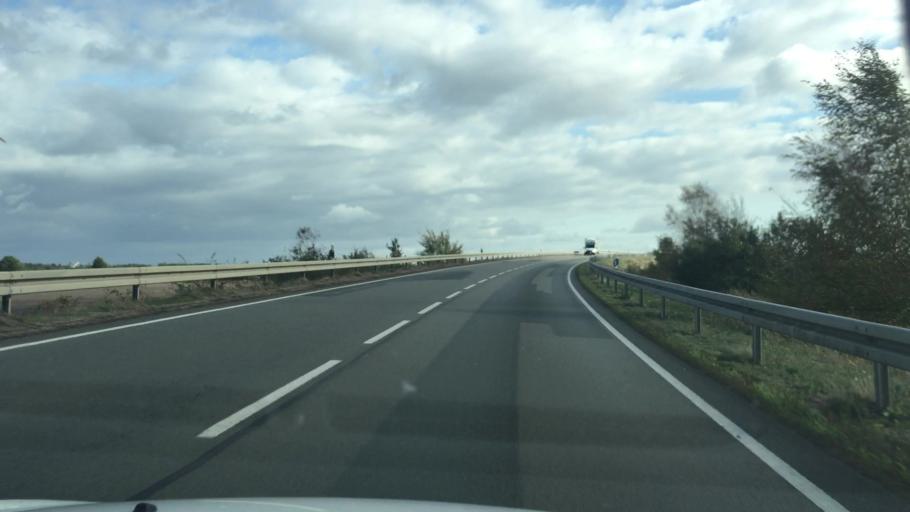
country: DE
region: Lower Saxony
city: Diepholz
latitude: 52.6265
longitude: 8.4065
